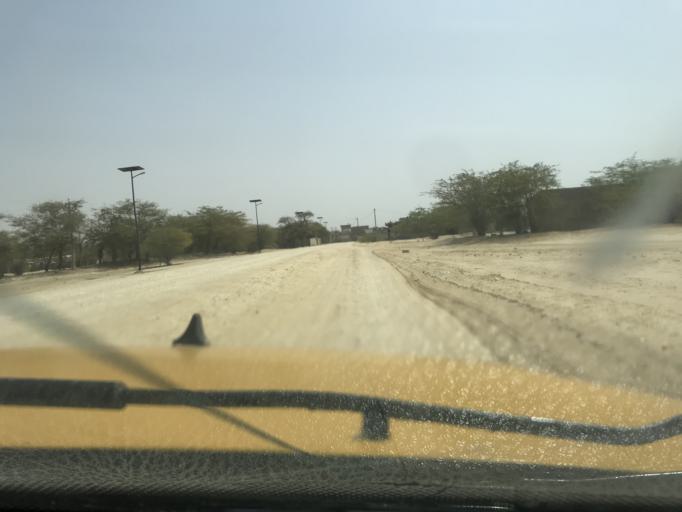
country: SN
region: Saint-Louis
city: Saint-Louis
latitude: 16.0222
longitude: -16.4464
